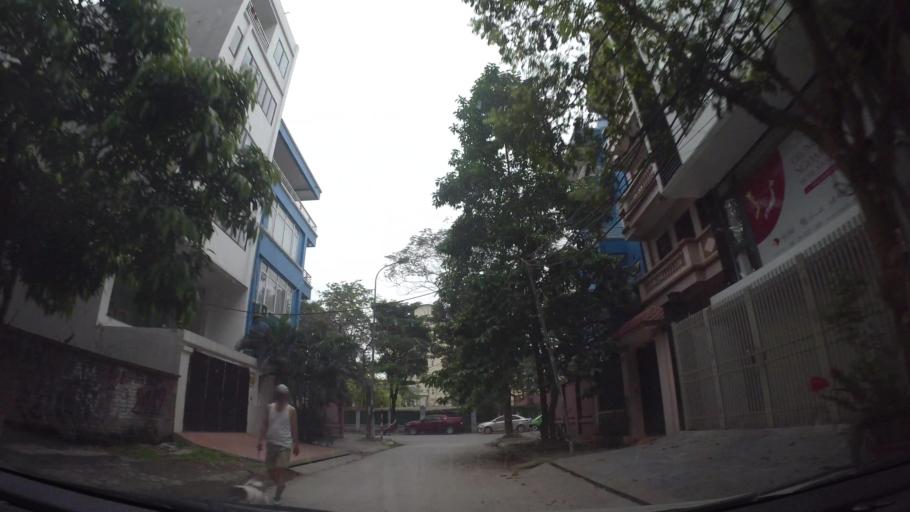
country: VN
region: Ha Noi
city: Cau Dien
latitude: 21.0383
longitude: 105.7657
